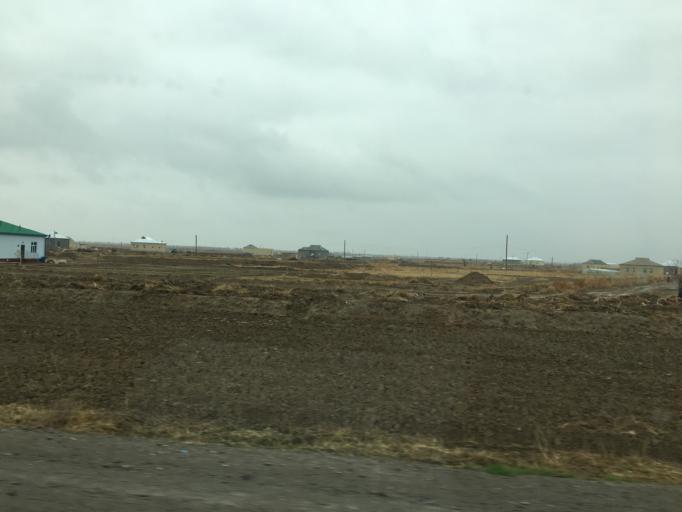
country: TM
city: Murgab
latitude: 37.4723
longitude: 62.0246
